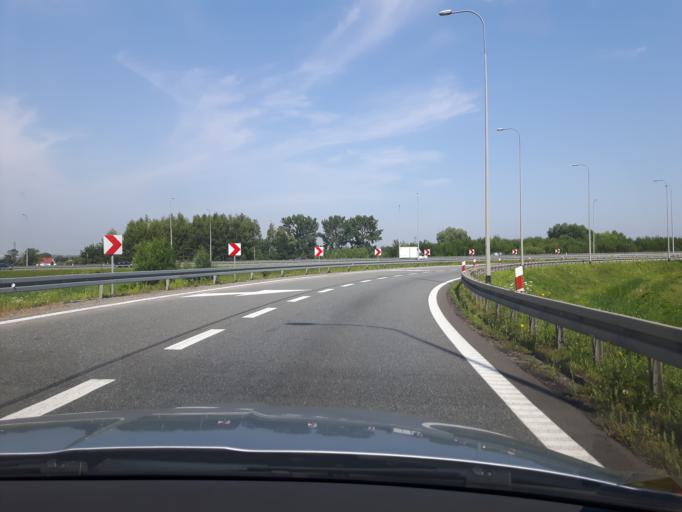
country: PL
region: Pomeranian Voivodeship
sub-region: Gdansk
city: Gdansk
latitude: 54.3175
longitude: 18.7022
